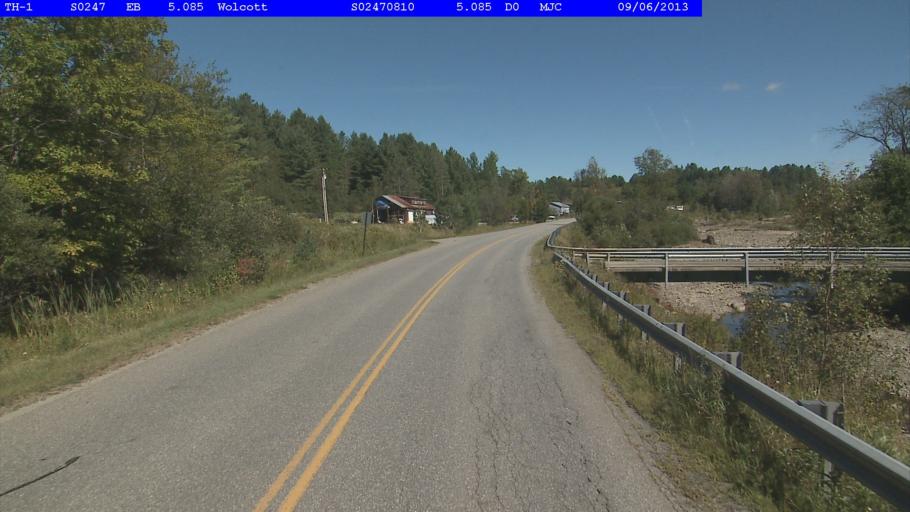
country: US
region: Vermont
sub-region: Caledonia County
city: Hardwick
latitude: 44.6183
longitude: -72.4460
